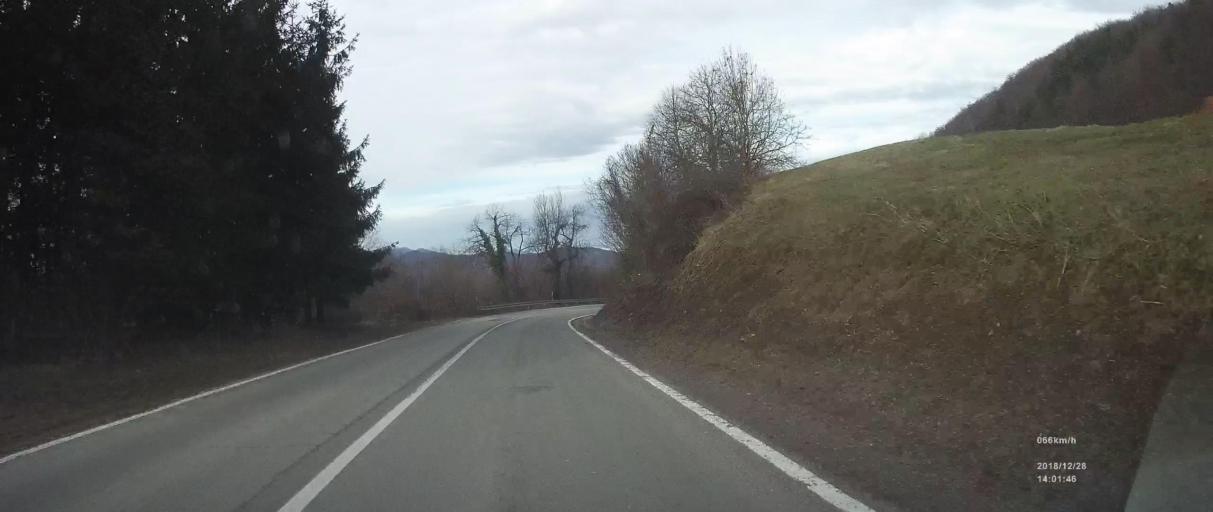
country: SI
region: Kostel
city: Kostel
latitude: 45.4235
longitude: 14.9066
